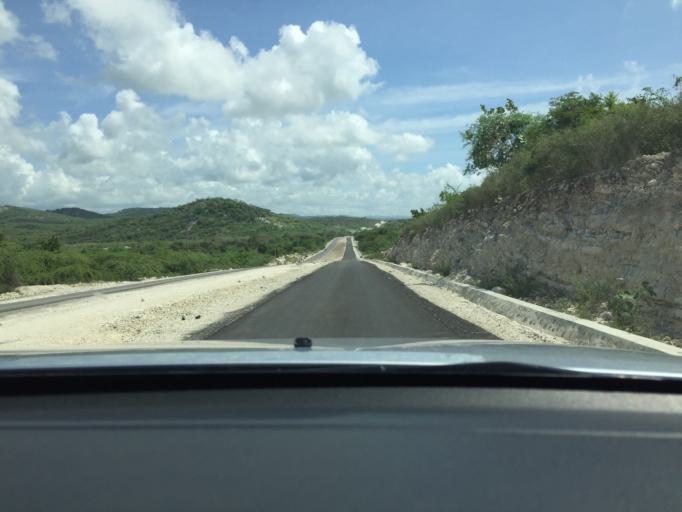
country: HT
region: Sud
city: Aquin
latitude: 18.2367
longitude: -73.2825
